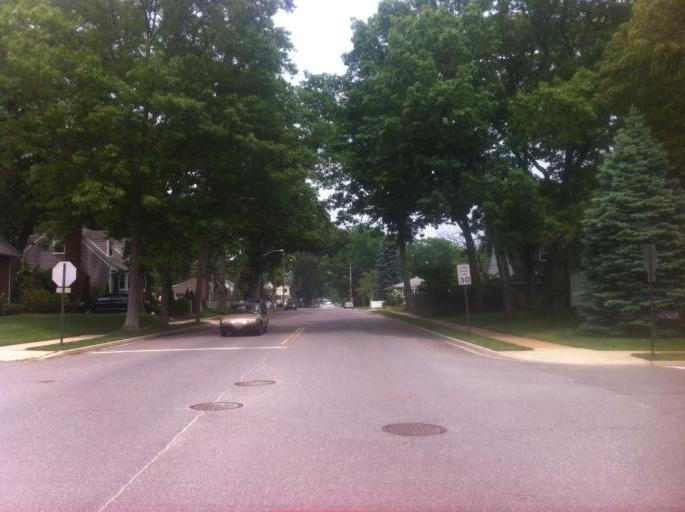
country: US
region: New York
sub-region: Nassau County
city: Massapequa
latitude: 40.6710
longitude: -73.4780
